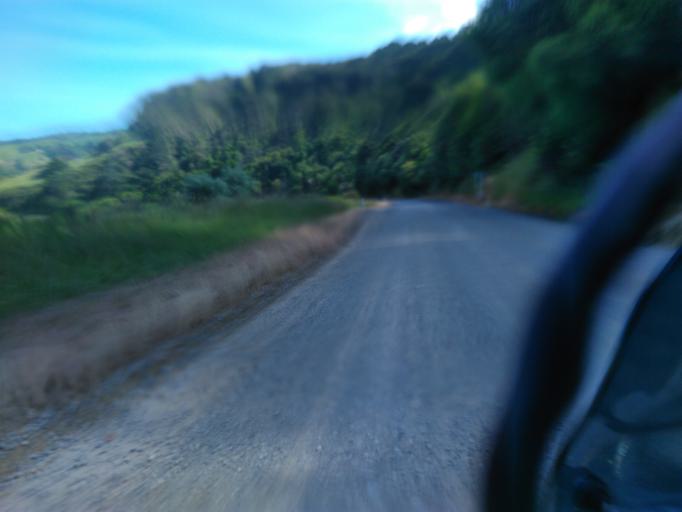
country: NZ
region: Hawke's Bay
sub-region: Wairoa District
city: Wairoa
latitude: -38.8669
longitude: 177.1990
